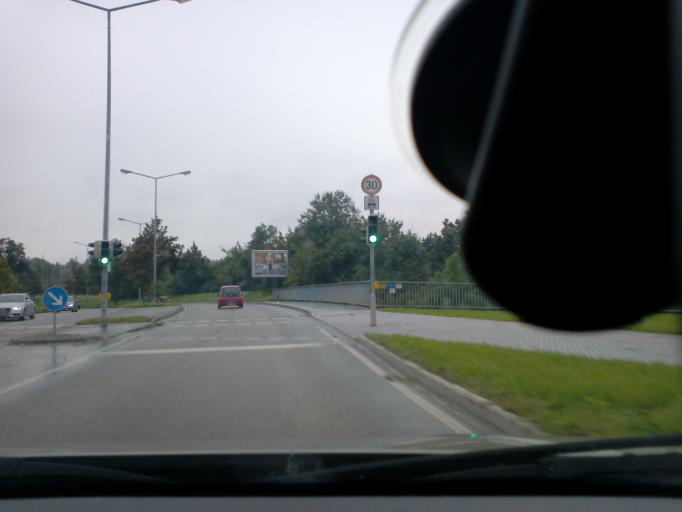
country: DE
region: Baden-Wuerttemberg
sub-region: Regierungsbezirk Stuttgart
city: Heilbronn
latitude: 49.1382
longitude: 9.2001
